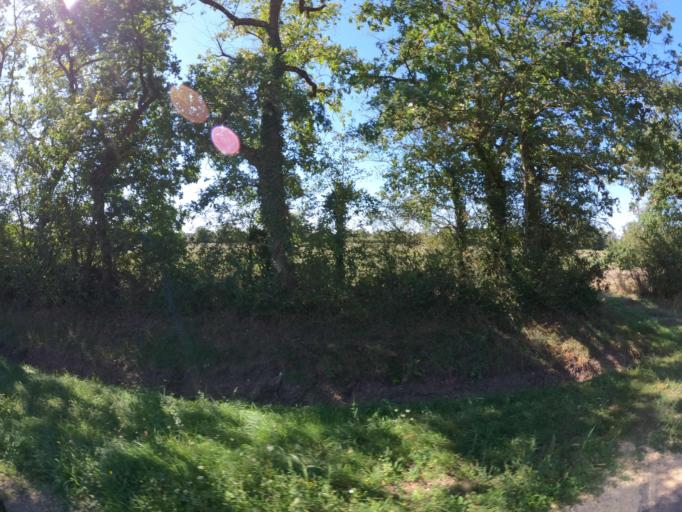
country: FR
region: Poitou-Charentes
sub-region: Departement de la Vienne
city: Saulge
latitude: 46.3927
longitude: 0.9053
